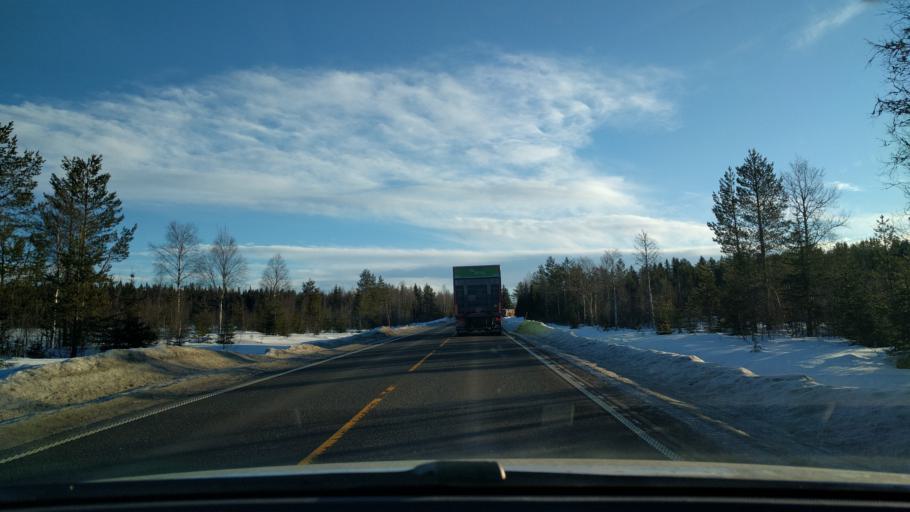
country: NO
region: Hedmark
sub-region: Trysil
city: Innbygda
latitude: 61.1171
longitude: 12.0540
